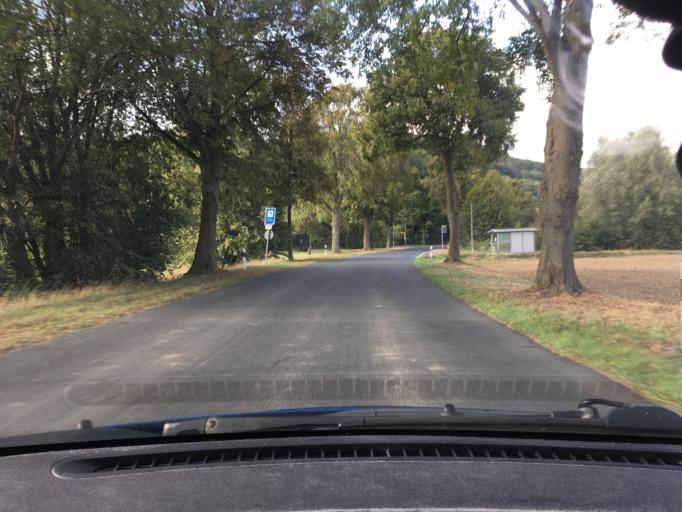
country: DE
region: Lower Saxony
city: Springe
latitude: 52.1979
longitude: 9.5274
